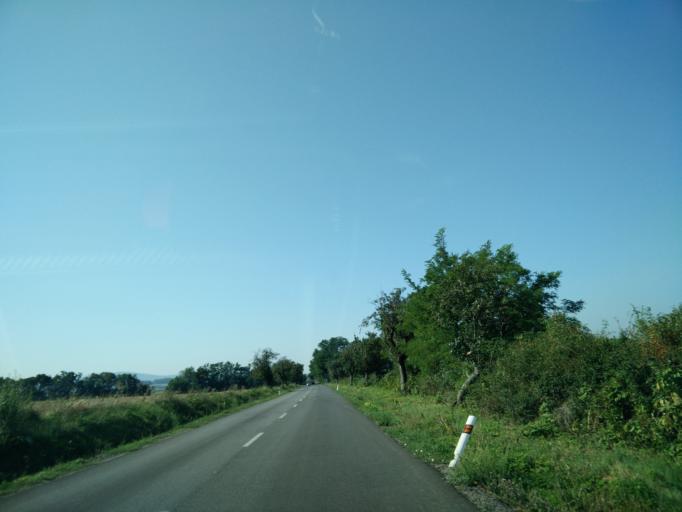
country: SK
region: Nitriansky
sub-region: Okres Nitra
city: Nitra
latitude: 48.4425
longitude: 18.1388
